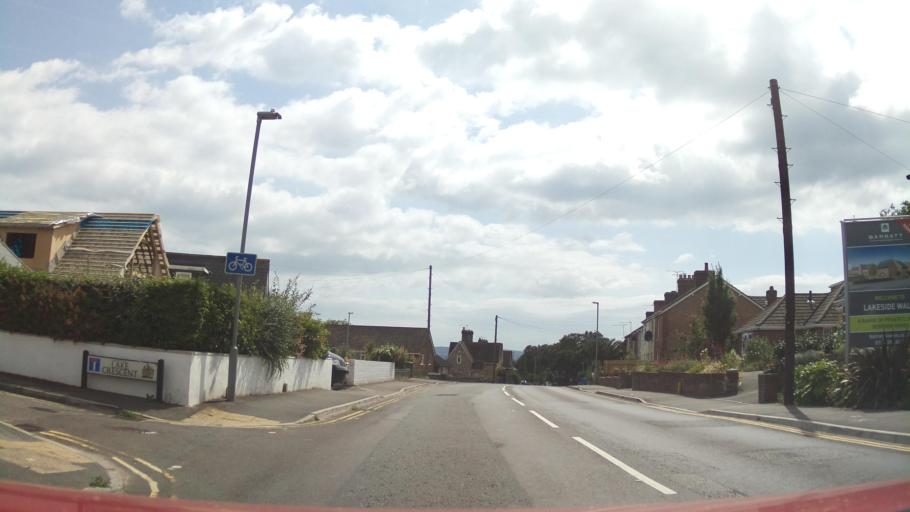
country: GB
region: England
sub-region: Poole
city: Poole
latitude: 50.7192
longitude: -2.0134
